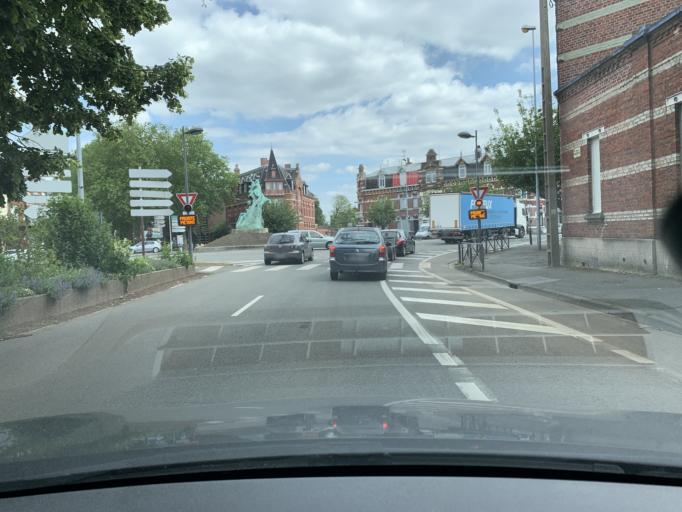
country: FR
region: Nord-Pas-de-Calais
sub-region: Departement du Nord
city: Douai
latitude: 50.3631
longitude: 3.0777
